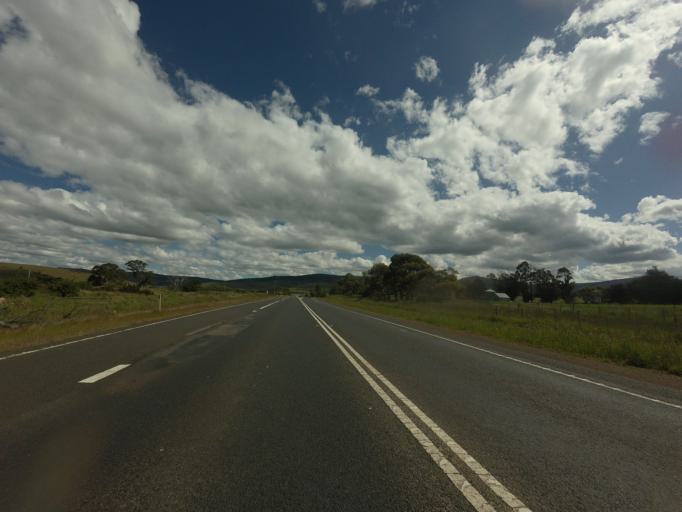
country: AU
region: Tasmania
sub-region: Brighton
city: Bridgewater
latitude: -42.1740
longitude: 147.3909
